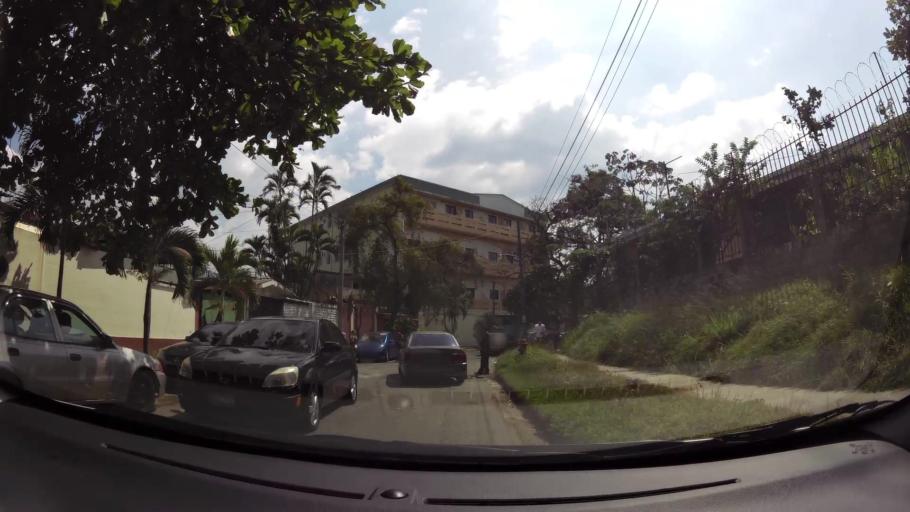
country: SV
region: San Salvador
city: Mejicanos
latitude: 13.7086
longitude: -89.2140
